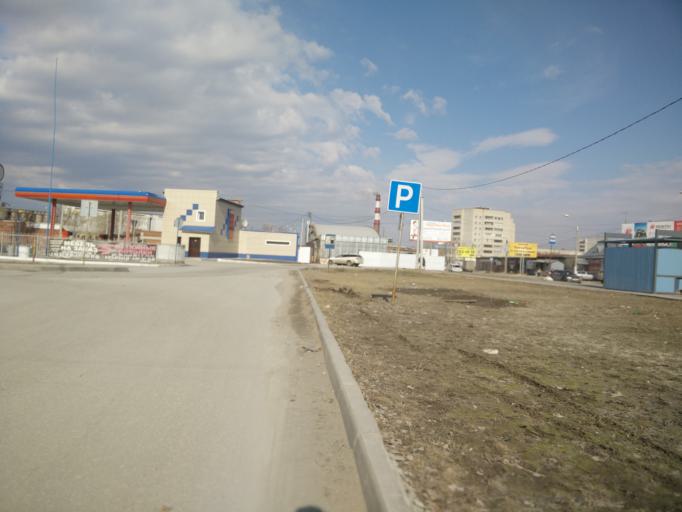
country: RU
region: Novosibirsk
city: Berdsk
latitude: 54.7655
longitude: 83.0830
